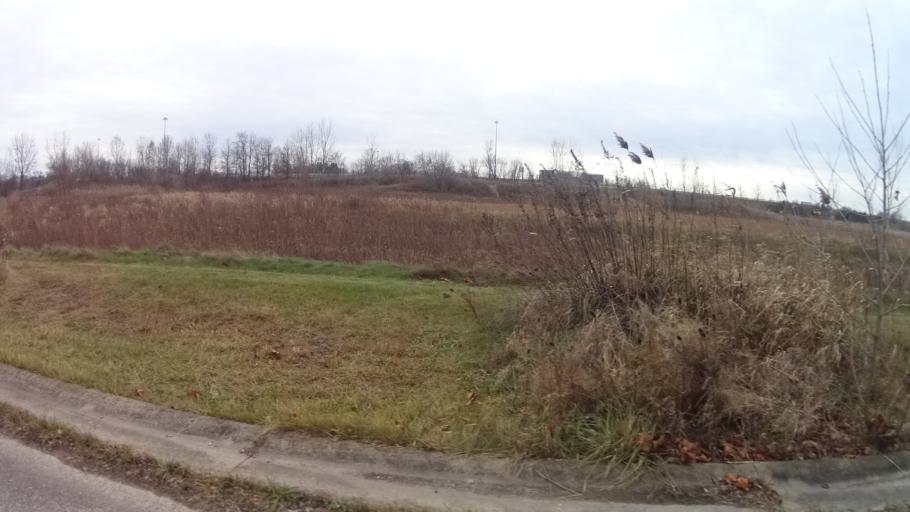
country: US
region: Ohio
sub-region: Lorain County
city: North Ridgeville
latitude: 41.3910
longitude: -81.9742
